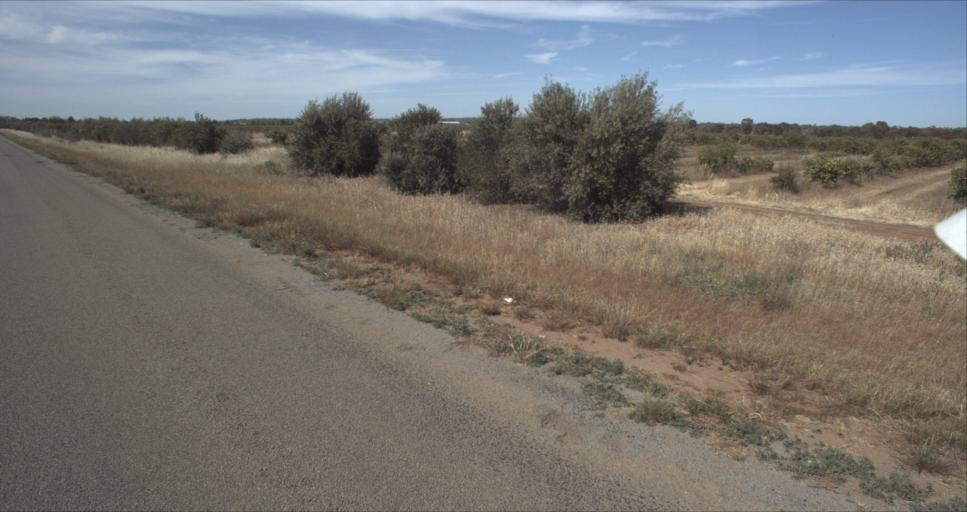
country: AU
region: New South Wales
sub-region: Leeton
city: Leeton
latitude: -34.5682
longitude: 146.4727
